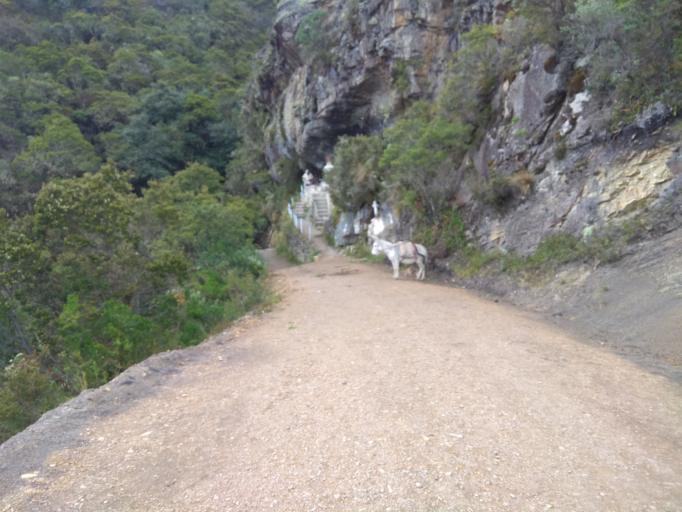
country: CO
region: Boyaca
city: Mongui
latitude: 5.7351
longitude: -72.8293
